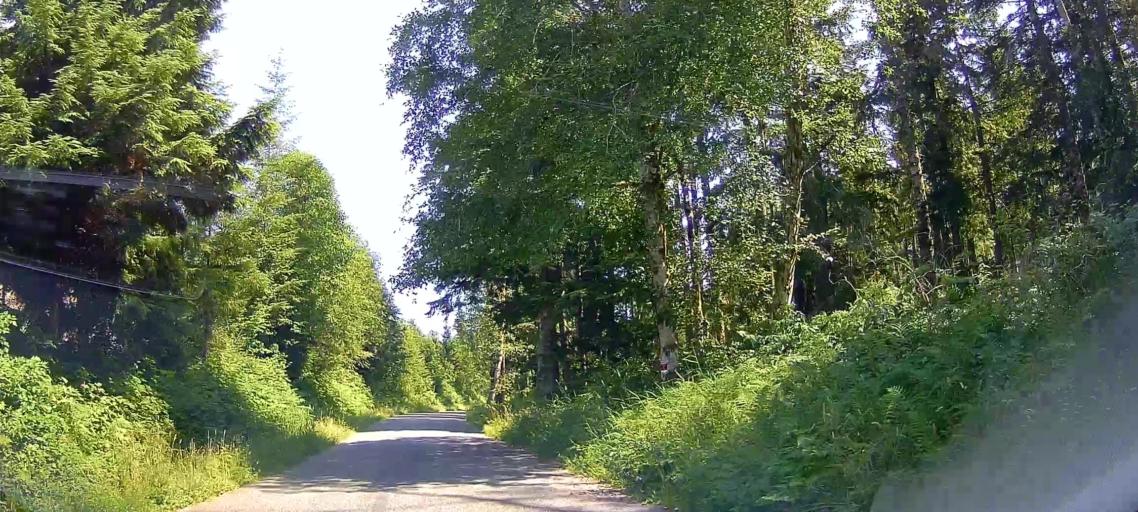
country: US
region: Washington
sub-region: Snohomish County
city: Arlington Heights
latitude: 48.3125
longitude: -121.9782
